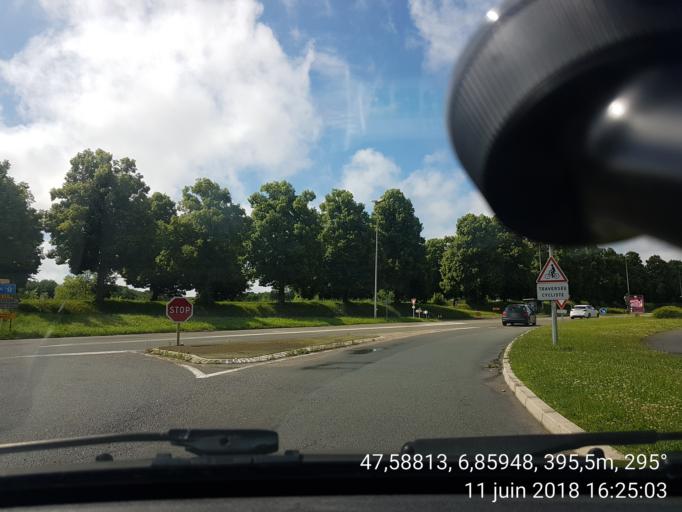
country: FR
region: Franche-Comte
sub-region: Territoire de Belfort
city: Andelnans
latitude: 47.5881
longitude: 6.8595
